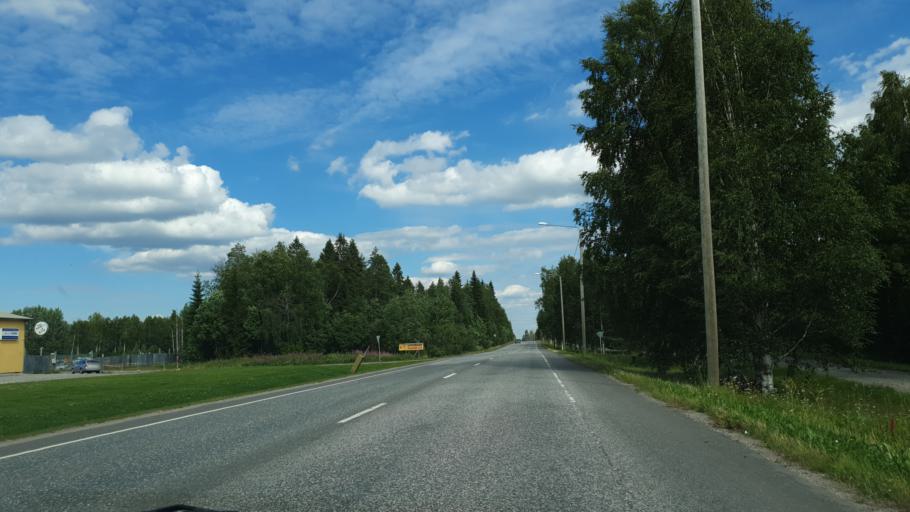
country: FI
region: Kainuu
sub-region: Kajaani
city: Kajaani
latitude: 64.2504
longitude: 27.7816
